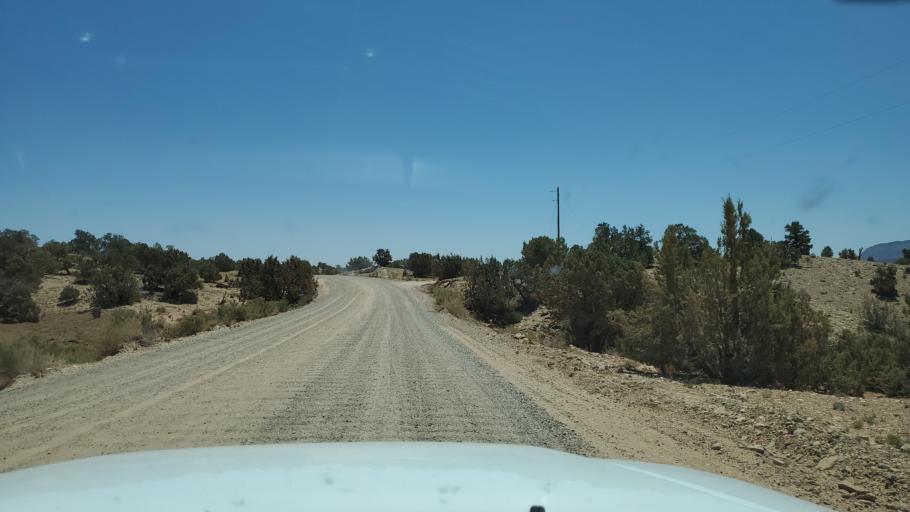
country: US
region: Utah
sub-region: Wayne County
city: Loa
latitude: 37.7254
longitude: -111.5289
